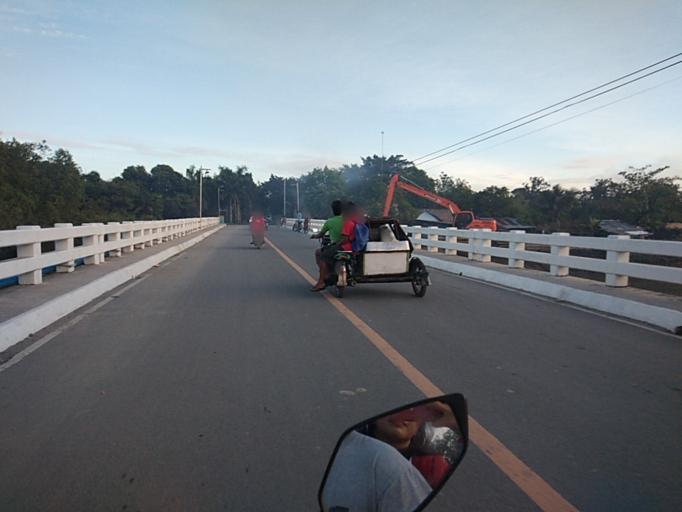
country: PH
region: Central Luzon
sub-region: Province of Bulacan
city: Paombong
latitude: 14.8601
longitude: 120.7656
